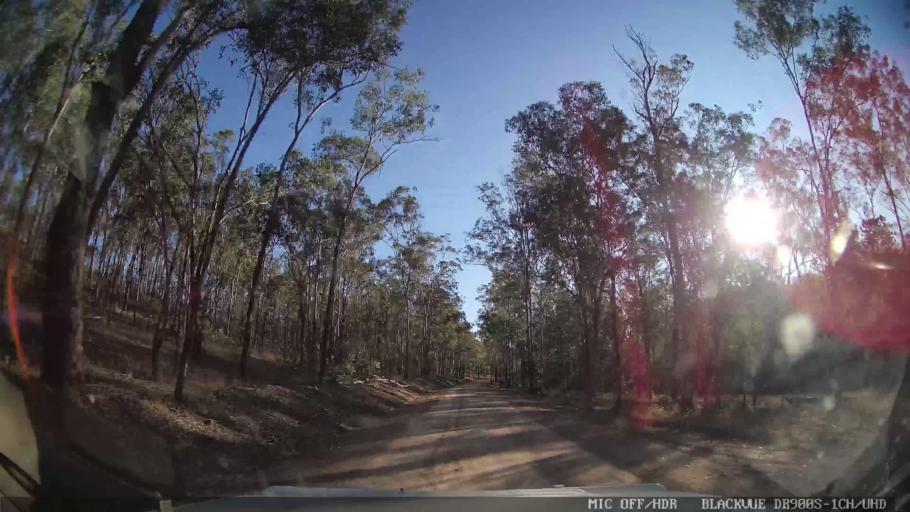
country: AU
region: Queensland
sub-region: Gladstone
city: Toolooa
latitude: -24.6950
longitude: 151.4106
